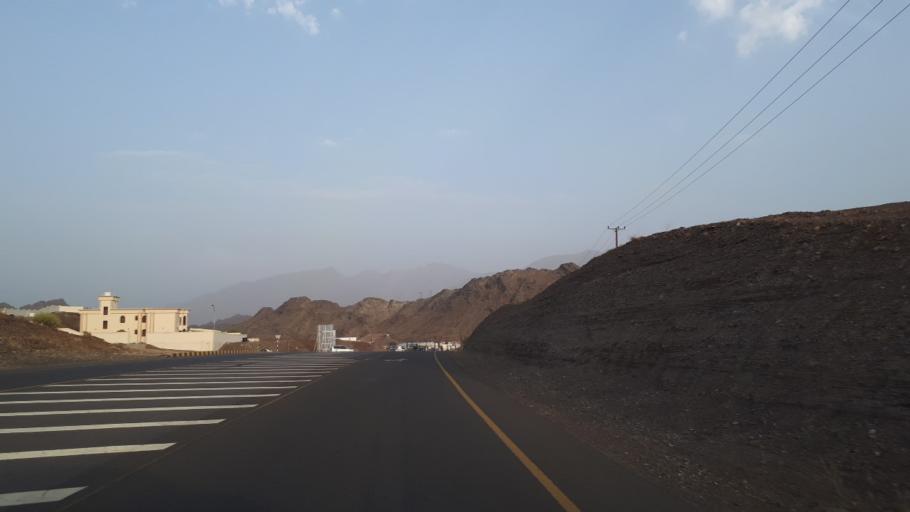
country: OM
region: Al Batinah
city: Rustaq
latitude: 23.4283
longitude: 57.2839
